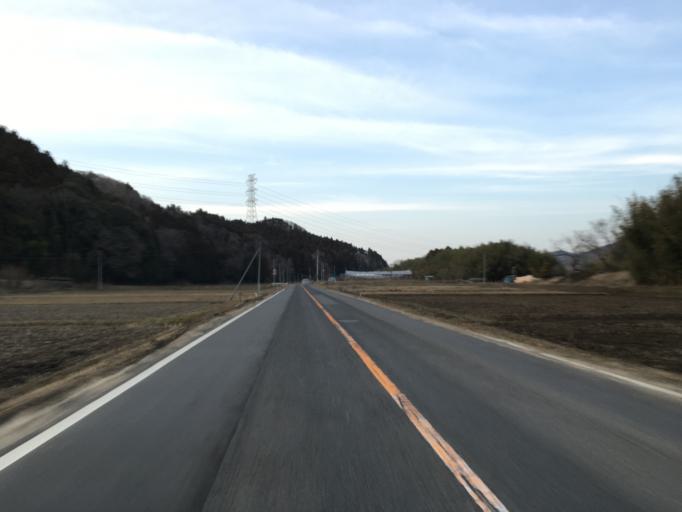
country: JP
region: Ibaraki
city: Daigo
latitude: 36.8862
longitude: 140.4120
